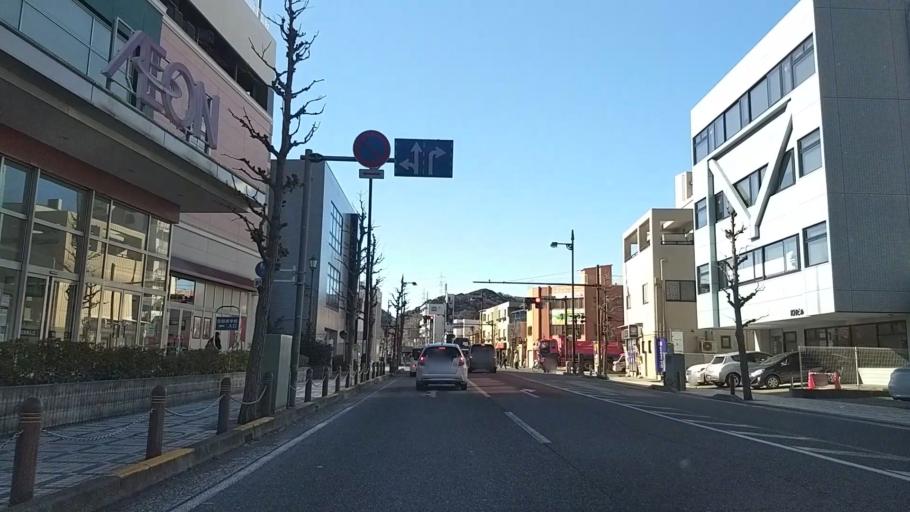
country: JP
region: Kanagawa
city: Yokosuka
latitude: 35.2296
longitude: 139.7037
